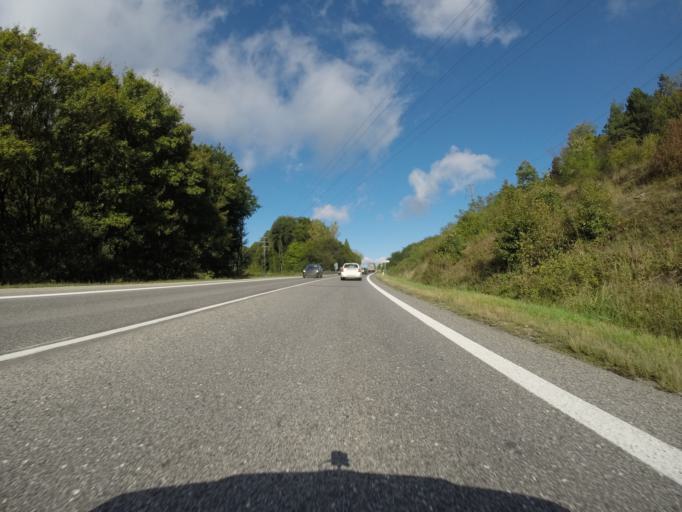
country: SK
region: Trenciansky
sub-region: Okres Trencin
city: Trencin
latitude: 48.8087
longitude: 18.0933
